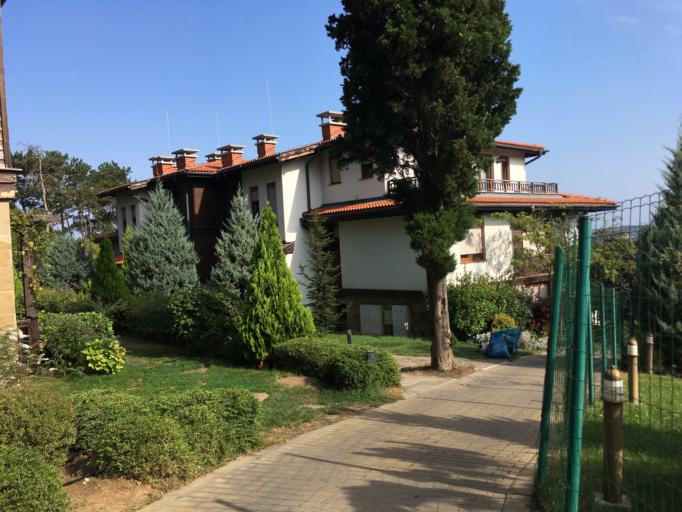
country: BG
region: Burgas
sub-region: Obshtina Sozopol
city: Sozopol
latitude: 42.4119
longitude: 27.6821
